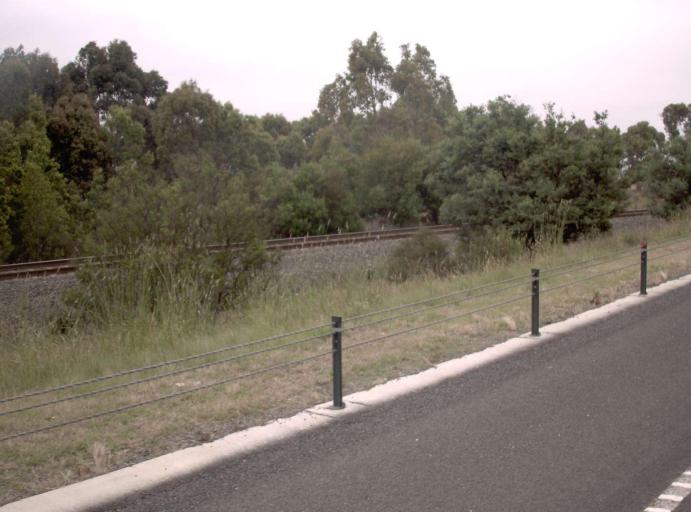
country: AU
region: Victoria
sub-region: Latrobe
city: Morwell
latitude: -38.2282
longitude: 146.4610
